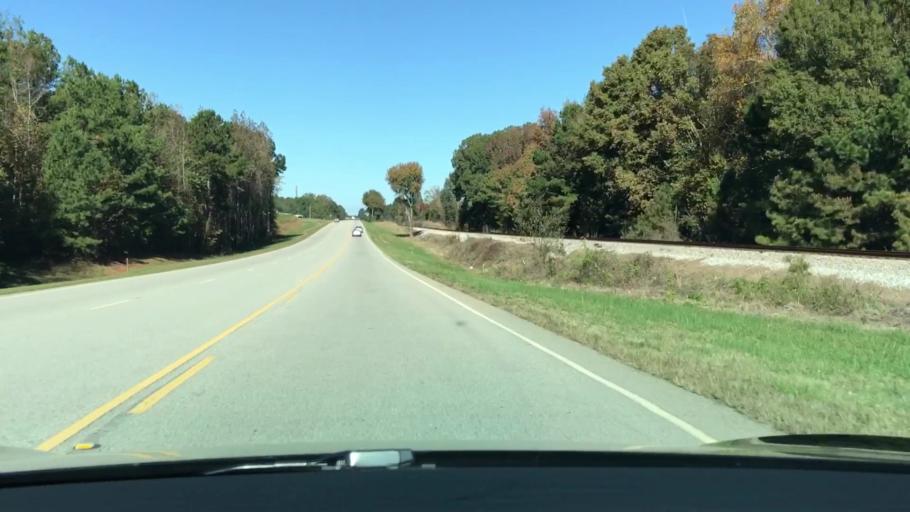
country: US
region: Georgia
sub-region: Warren County
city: Firing Range
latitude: 33.4880
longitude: -82.7962
